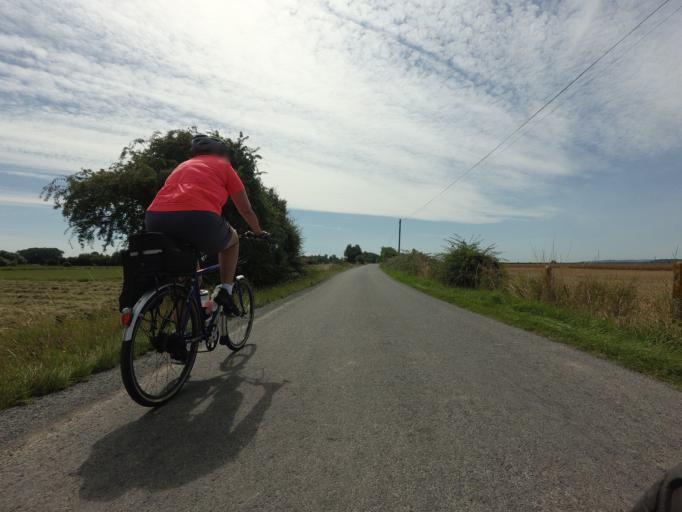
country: GB
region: England
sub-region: Kent
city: Stone
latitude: 51.0005
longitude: 0.8031
